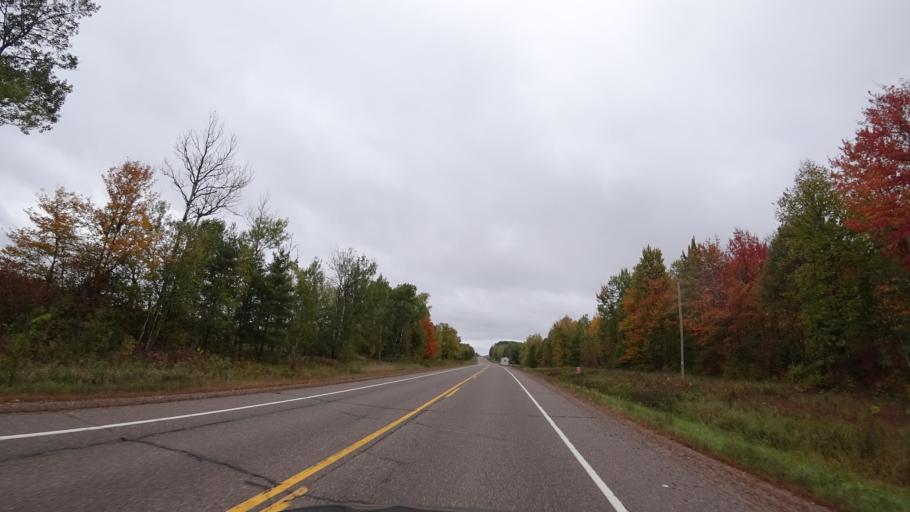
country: US
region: Wisconsin
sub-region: Rusk County
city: Ladysmith
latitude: 45.5718
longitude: -91.1116
